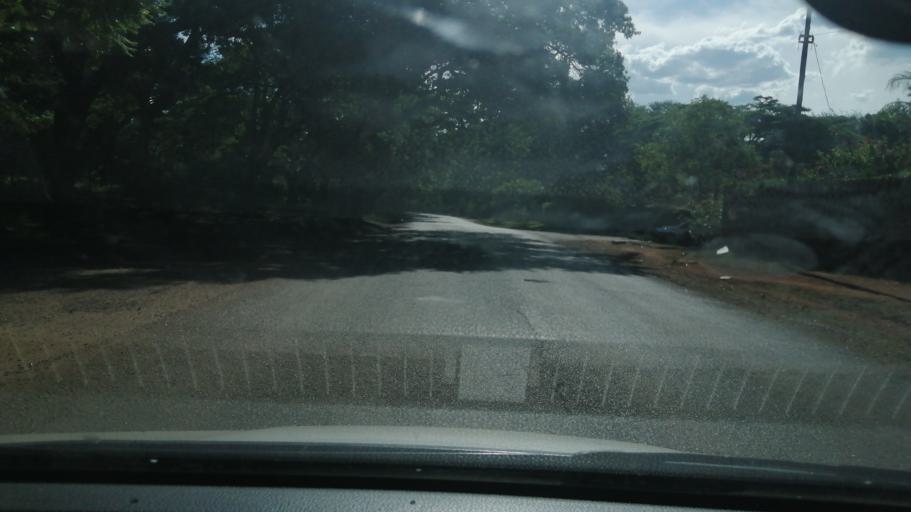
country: ZW
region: Harare
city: Harare
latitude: -17.7957
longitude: 31.0534
